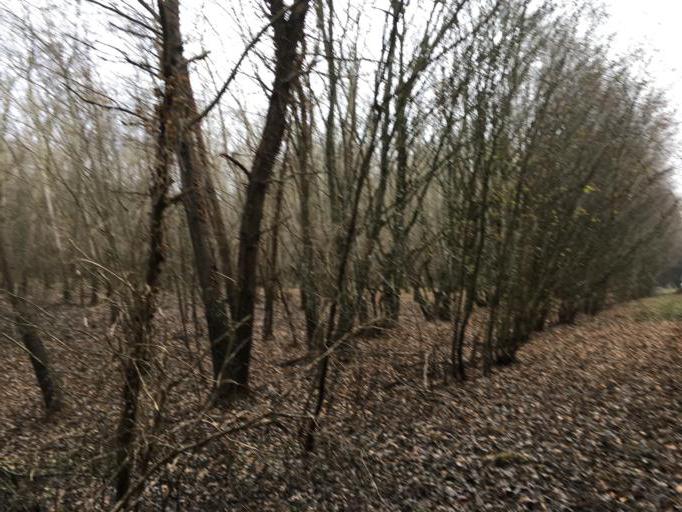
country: FR
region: Centre
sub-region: Departement du Loiret
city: Saran
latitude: 47.9844
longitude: 1.8939
